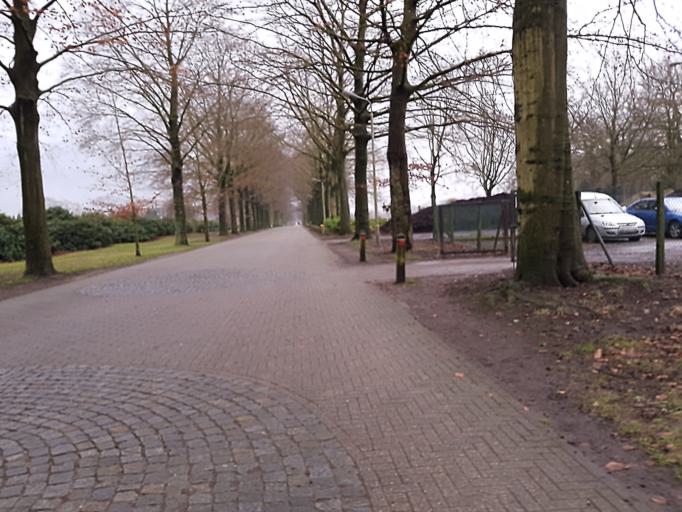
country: BE
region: Flanders
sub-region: Provincie Antwerpen
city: Borsbeek
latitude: 51.2174
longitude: 4.4734
